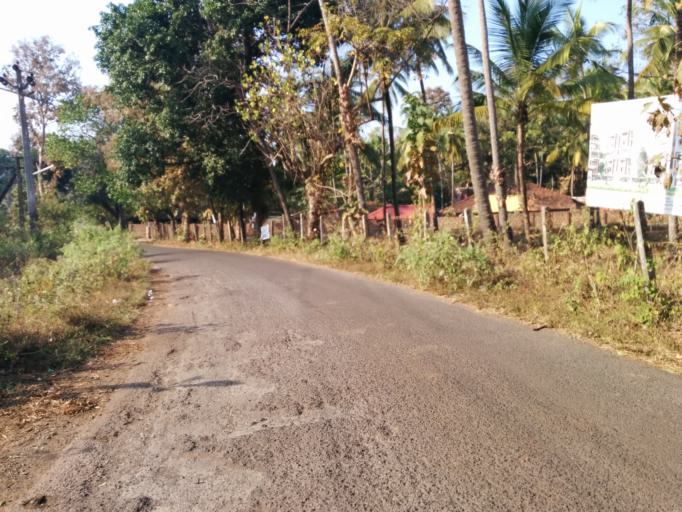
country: IN
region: Karnataka
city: Canacona
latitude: 15.0065
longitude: 74.0311
